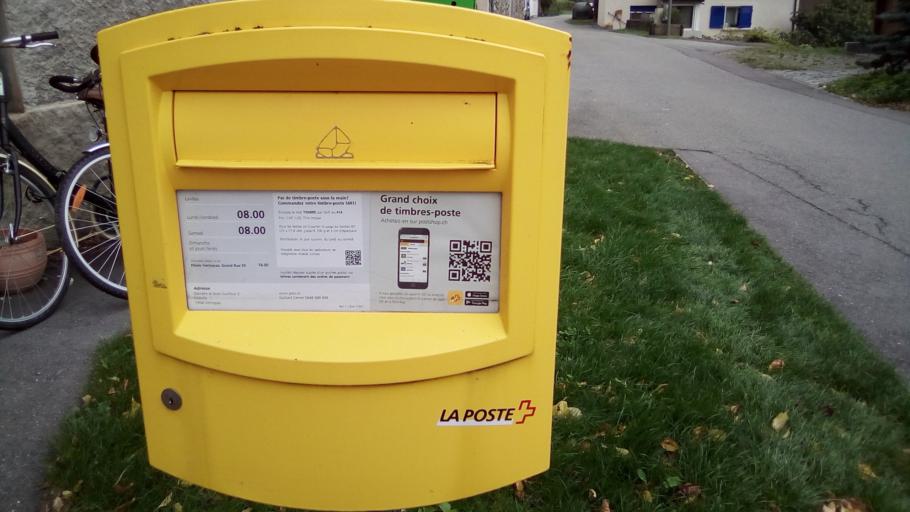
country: CH
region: Valais
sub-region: Saint-Maurice District
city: Vernayaz
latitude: 46.1483
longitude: 7.0295
